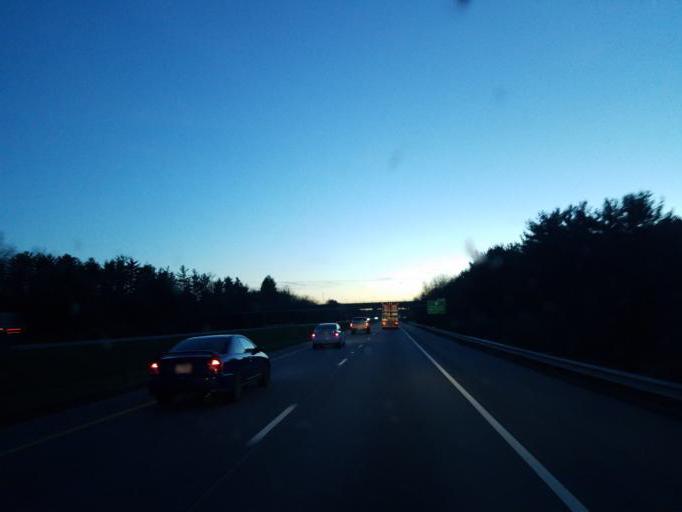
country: US
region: Ohio
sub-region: Muskingum County
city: New Concord
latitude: 39.9848
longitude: -81.7143
